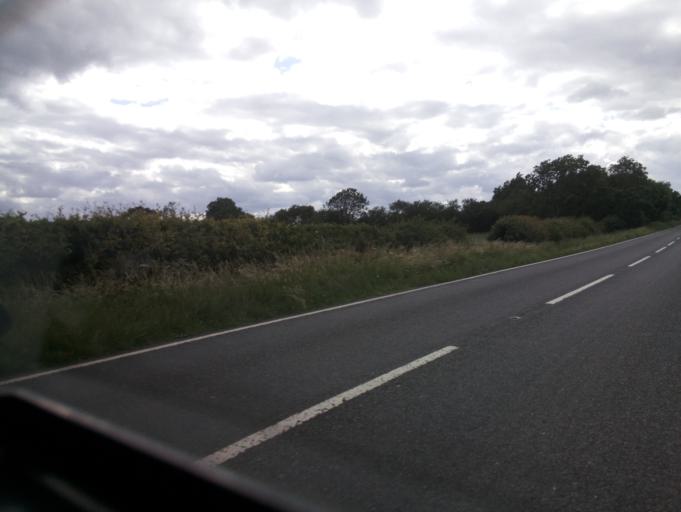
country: GB
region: England
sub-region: Leicestershire
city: Measham
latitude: 52.6520
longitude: -1.5169
